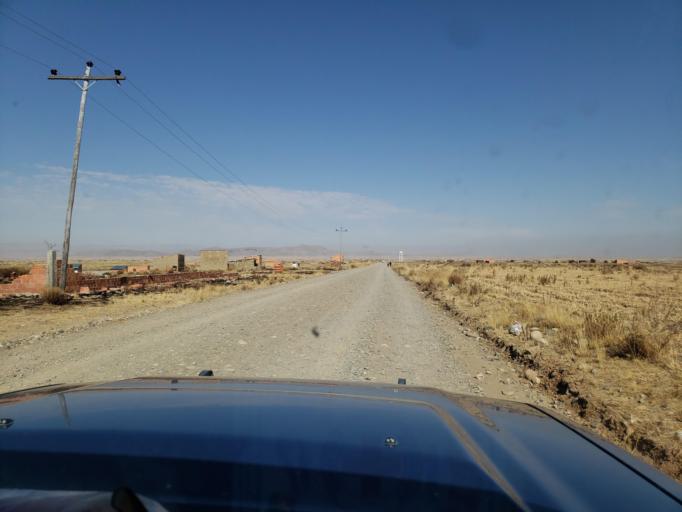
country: BO
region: La Paz
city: La Paz
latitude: -16.4306
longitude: -68.3349
